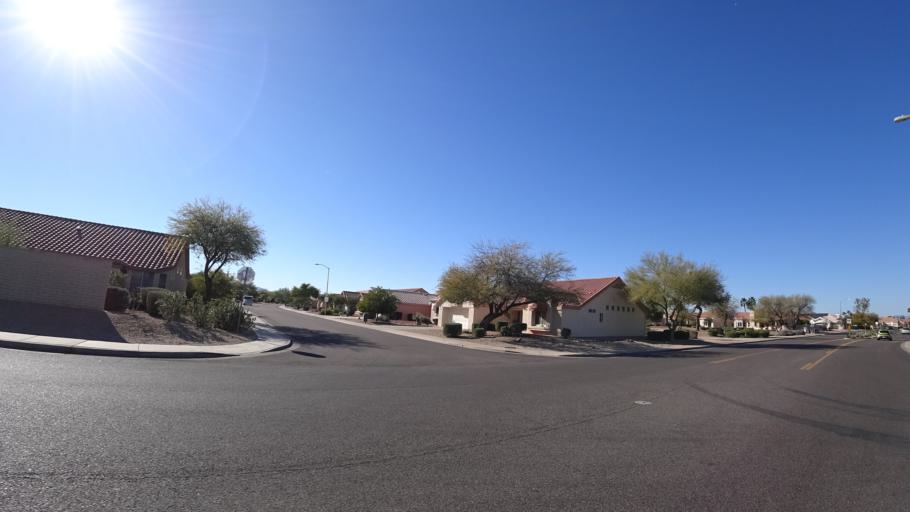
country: US
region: Arizona
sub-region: Maricopa County
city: Sun City West
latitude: 33.6741
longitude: -112.3800
